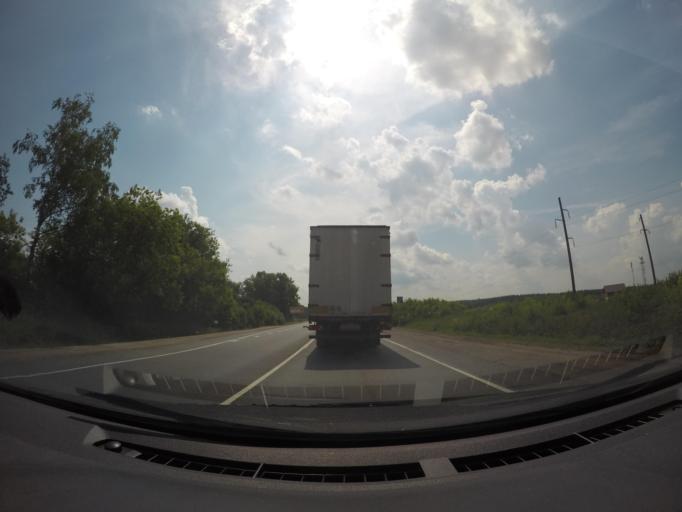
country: RU
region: Moskovskaya
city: Malyshevo
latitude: 55.4875
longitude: 38.3418
